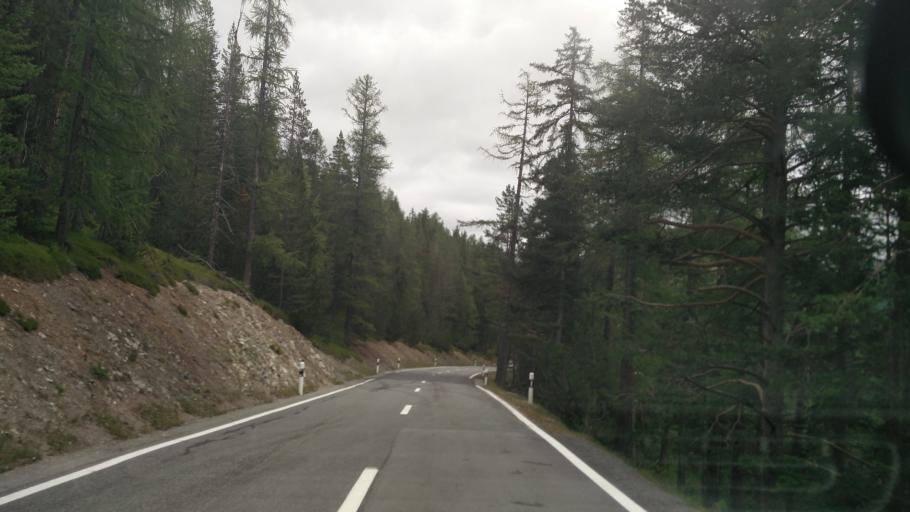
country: CH
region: Grisons
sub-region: Inn District
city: Zernez
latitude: 46.6657
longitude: 10.1681
